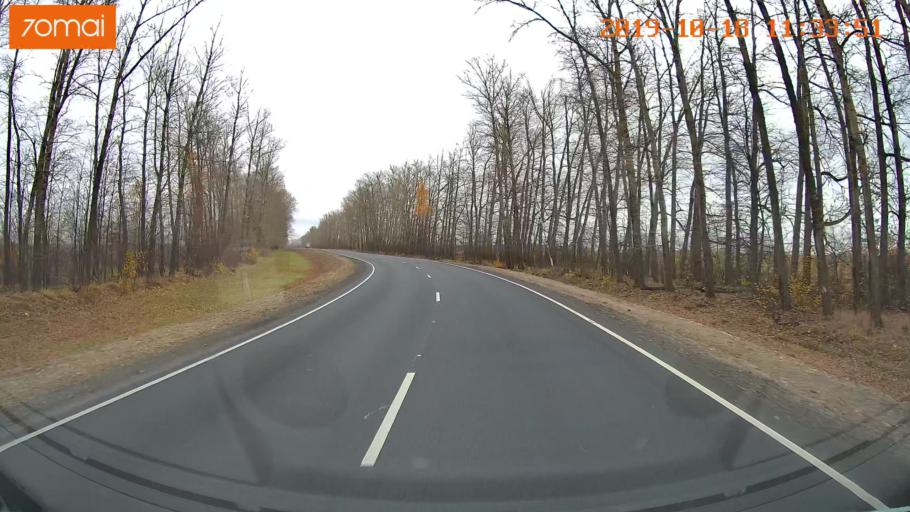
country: RU
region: Rjazan
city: Oktyabr'skiy
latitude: 54.1379
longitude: 38.7503
